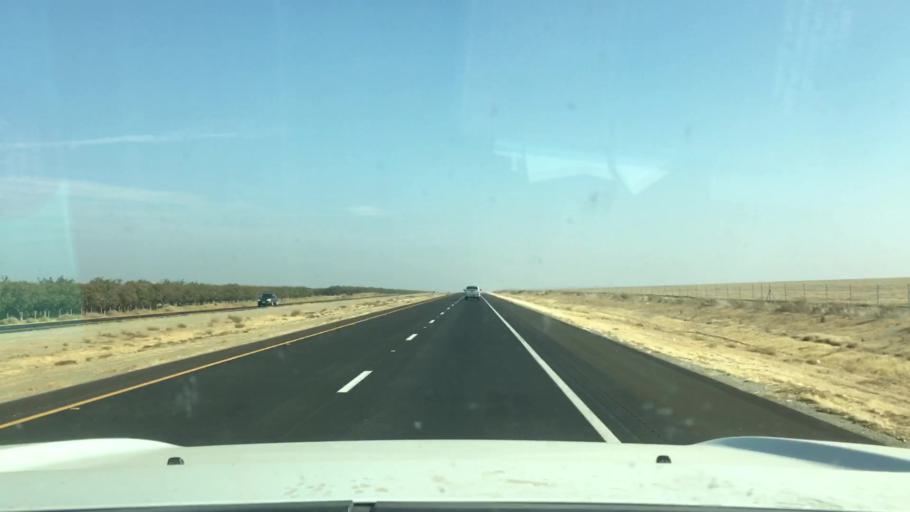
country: US
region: California
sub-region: Kern County
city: Lost Hills
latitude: 35.6143
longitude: -119.9438
